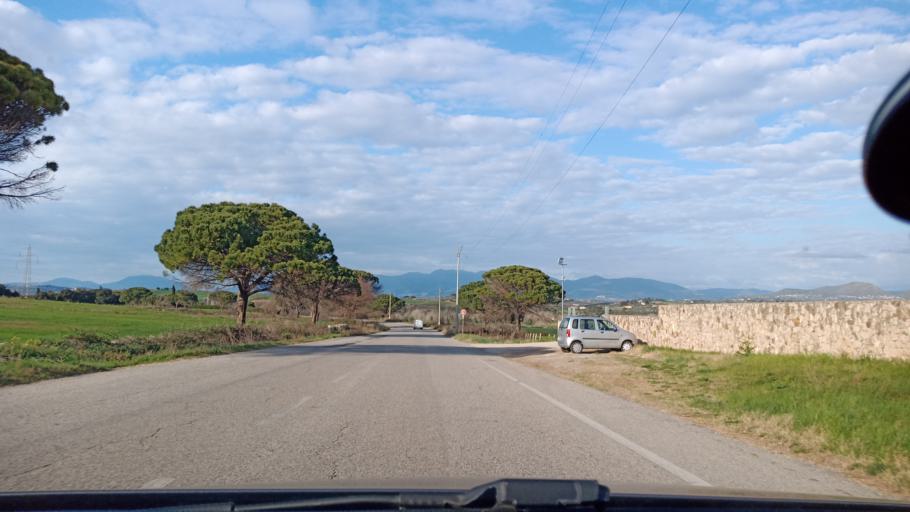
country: IT
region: Latium
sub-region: Citta metropolitana di Roma Capitale
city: Fiano Romano
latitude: 42.1620
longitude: 12.6206
